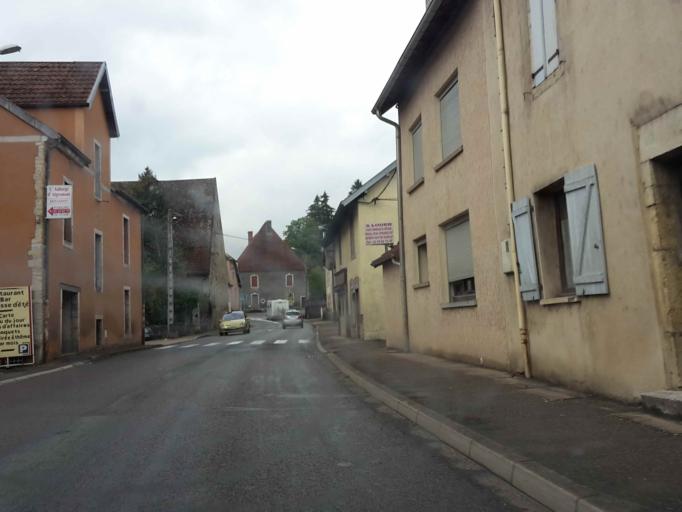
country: FR
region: Franche-Comte
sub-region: Departement du Doubs
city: Roulans
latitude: 47.3159
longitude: 6.2316
